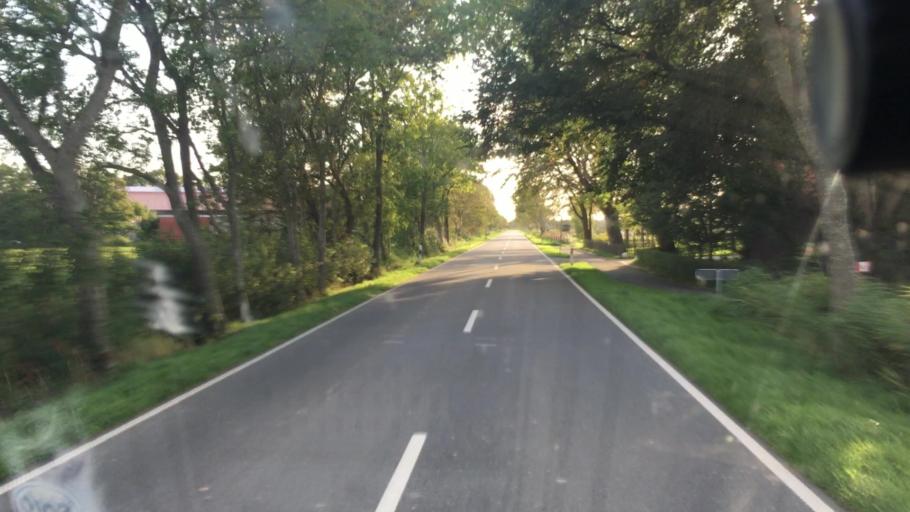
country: DE
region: Lower Saxony
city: Esens
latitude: 53.6810
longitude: 7.6029
